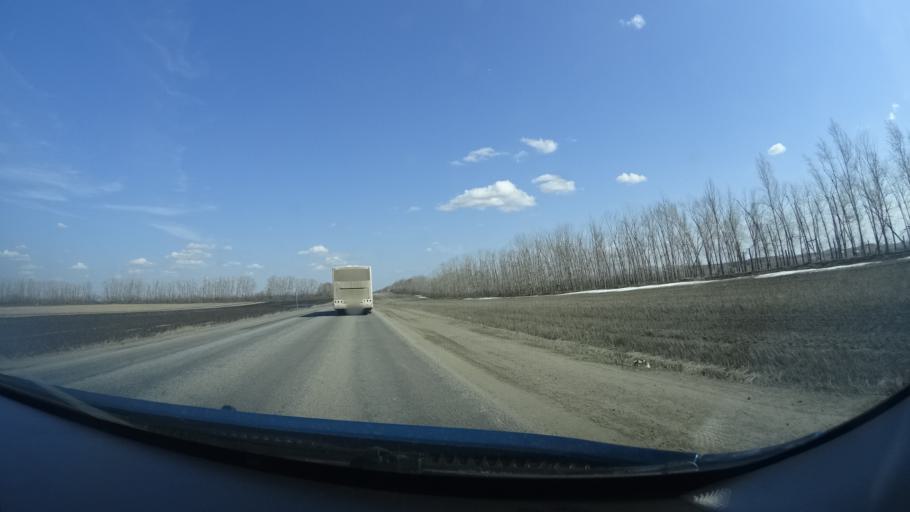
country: RU
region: Bashkortostan
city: Buzdyak
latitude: 54.6146
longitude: 54.3357
